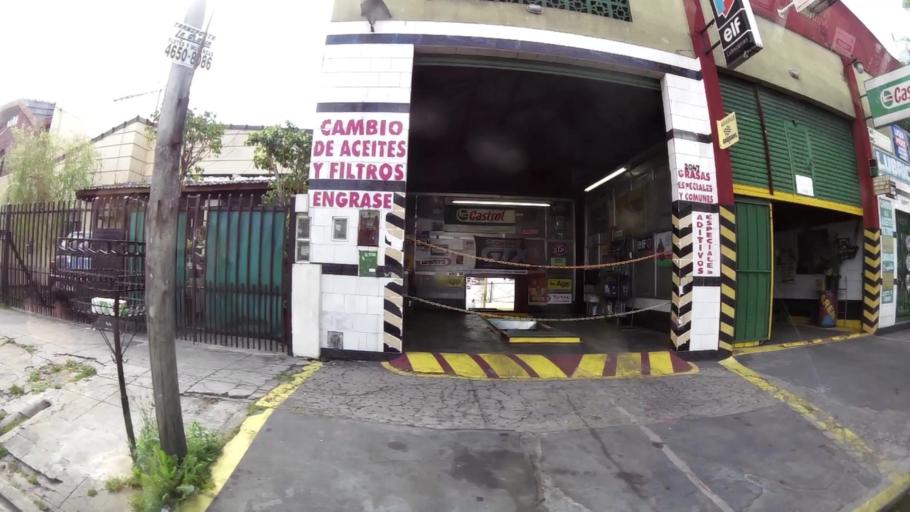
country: AR
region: Buenos Aires
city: San Justo
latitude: -34.6570
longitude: -58.5810
